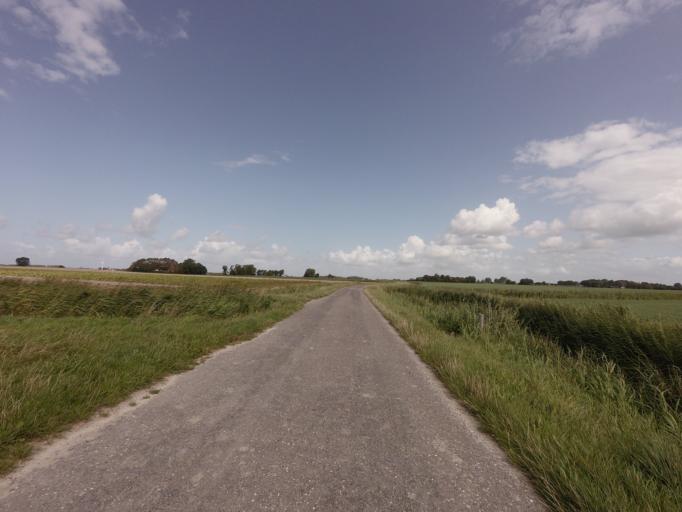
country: NL
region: Friesland
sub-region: Gemeente Harlingen
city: Harlingen
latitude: 53.1190
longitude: 5.4388
